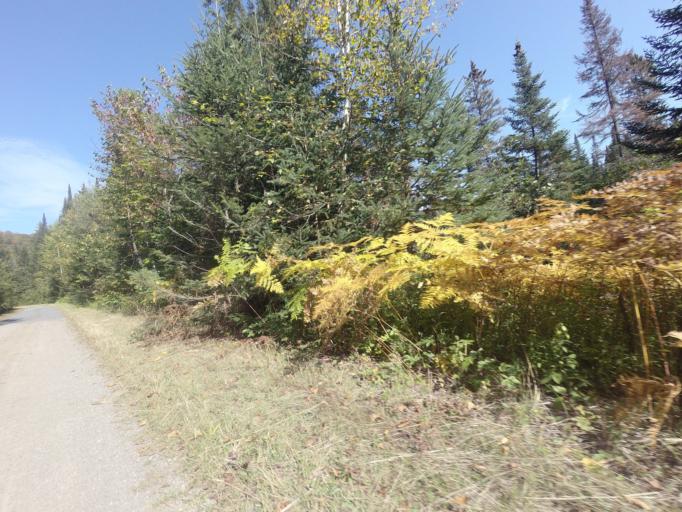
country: CA
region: Quebec
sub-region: Laurentides
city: Sainte-Agathe-des-Monts
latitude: 46.1022
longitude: -74.3638
